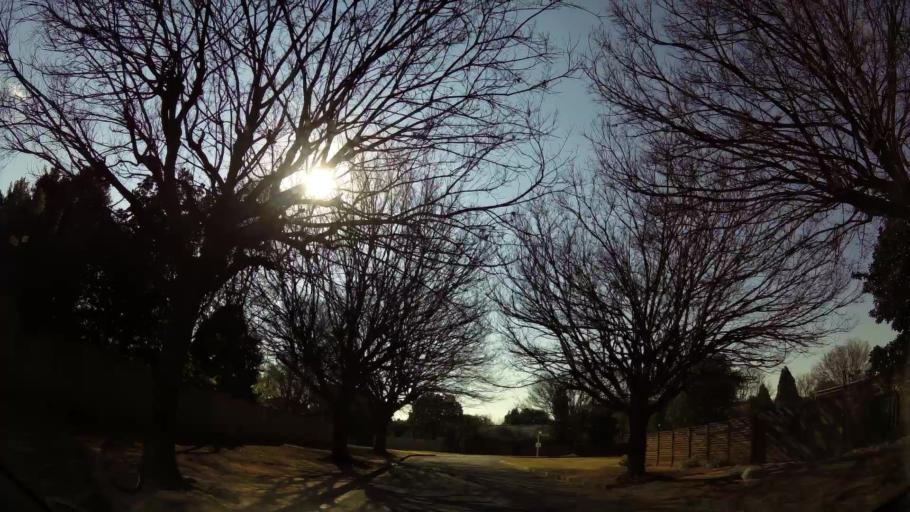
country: ZA
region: Gauteng
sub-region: Ekurhuleni Metropolitan Municipality
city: Benoni
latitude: -26.1511
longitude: 28.3219
